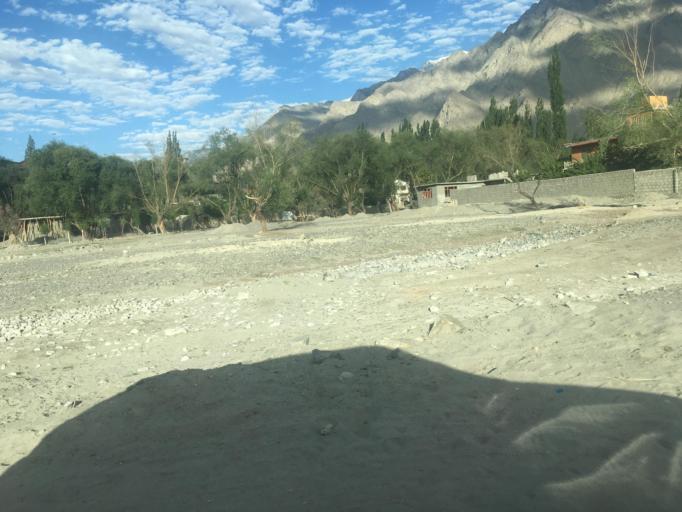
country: PK
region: Gilgit-Baltistan
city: Skardu
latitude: 35.2996
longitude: 75.6275
